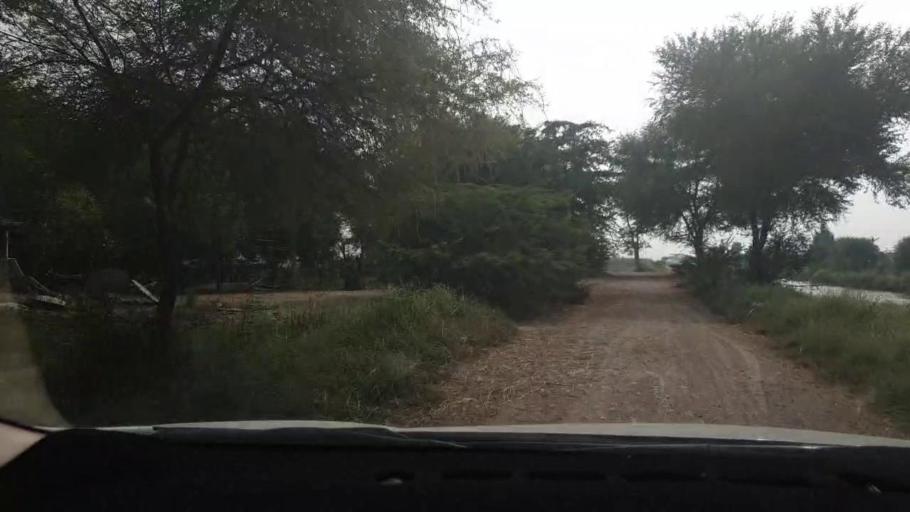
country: PK
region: Sindh
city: Tando Muhammad Khan
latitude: 25.0585
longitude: 68.5085
